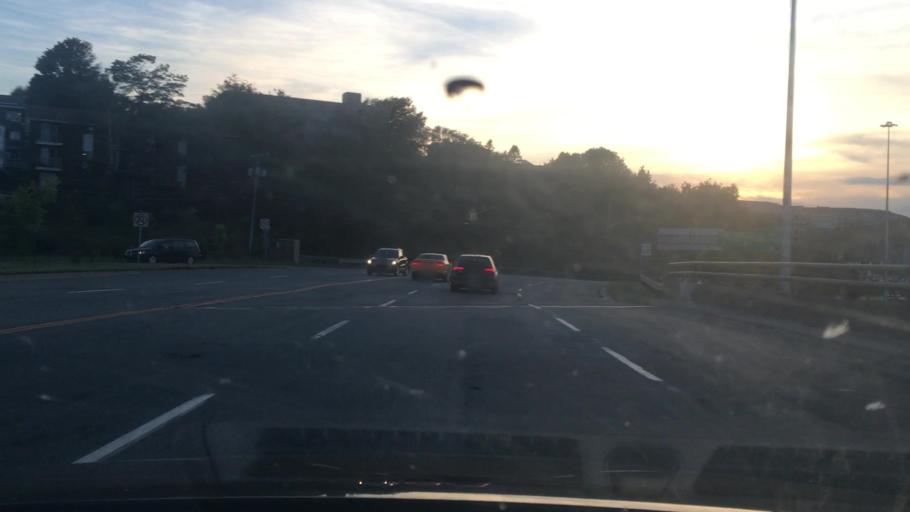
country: CA
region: Nova Scotia
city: Dartmouth
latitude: 44.6625
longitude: -63.6286
